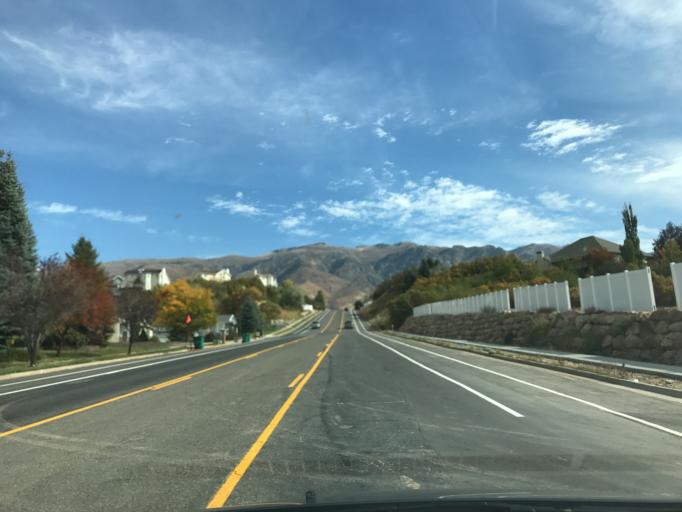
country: US
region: Utah
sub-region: Davis County
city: Layton
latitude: 41.0889
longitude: -111.9377
